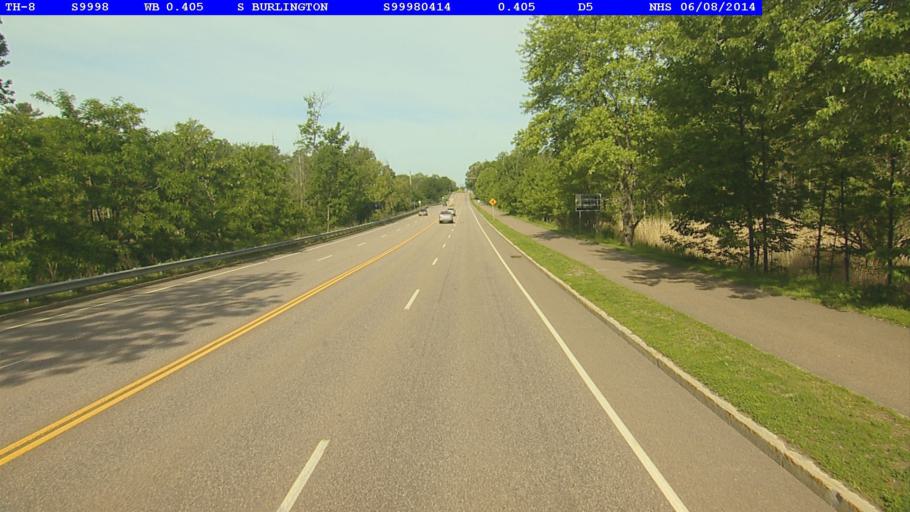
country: US
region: Vermont
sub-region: Chittenden County
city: South Burlington
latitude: 44.4537
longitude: -73.1706
